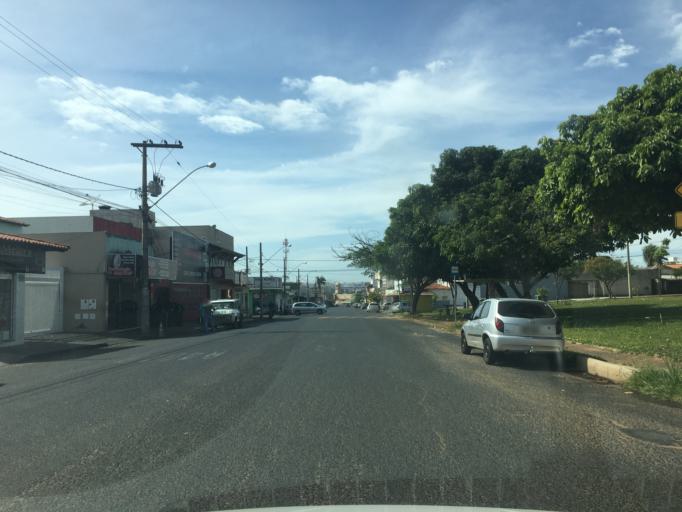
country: BR
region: Minas Gerais
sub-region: Uberlandia
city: Uberlandia
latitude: -18.9385
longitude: -48.3041
